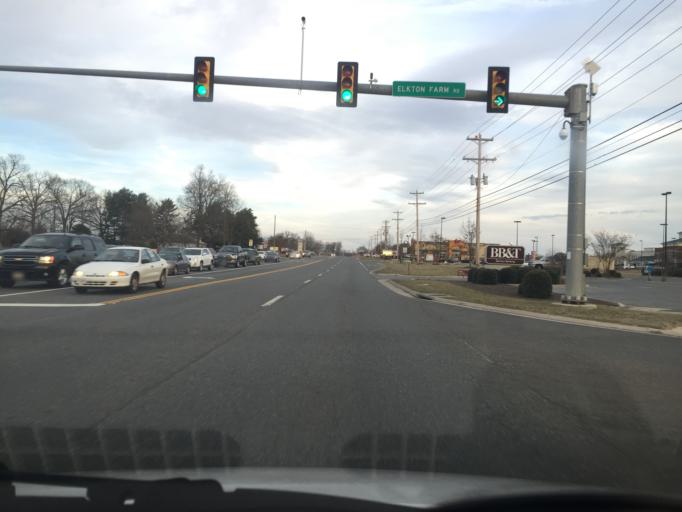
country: US
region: Virginia
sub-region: Bedford County
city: Forest
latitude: 37.3673
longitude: -79.2976
